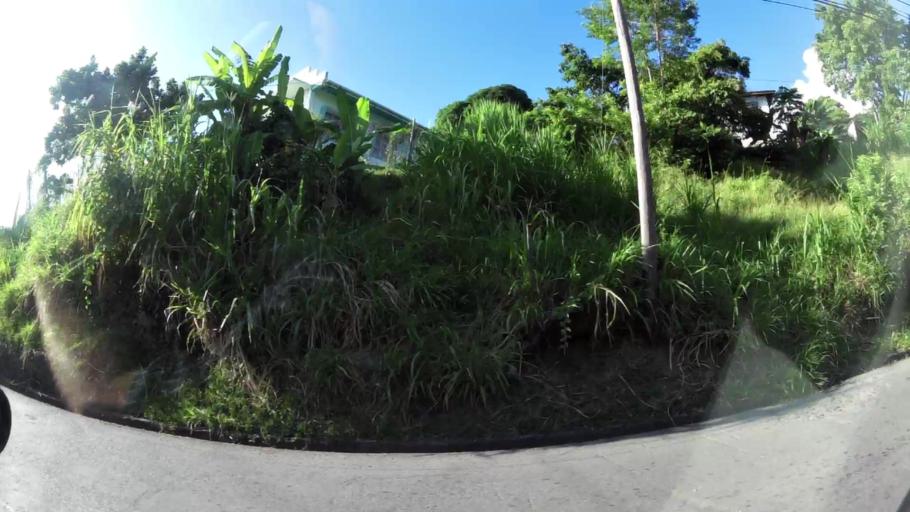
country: TT
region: Tobago
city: Scarborough
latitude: 11.1930
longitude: -60.6837
